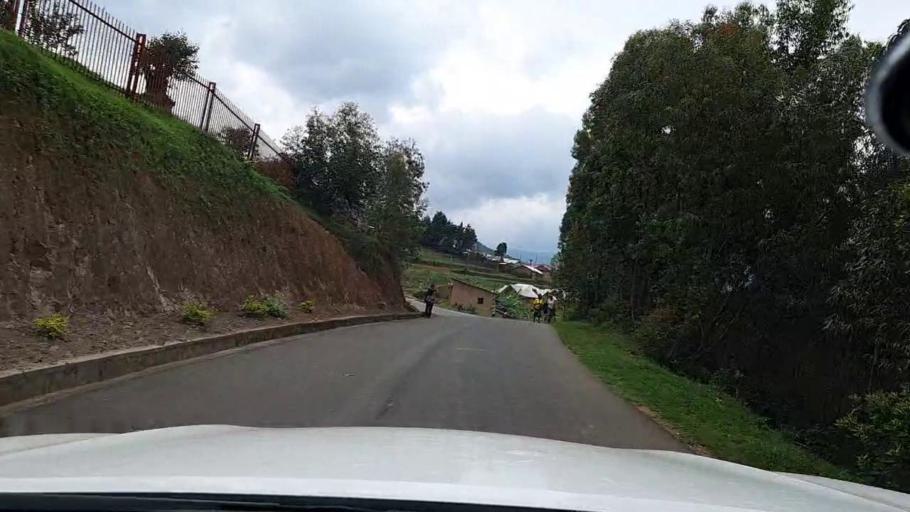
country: RW
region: Western Province
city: Kibuye
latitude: -2.1817
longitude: 29.2921
